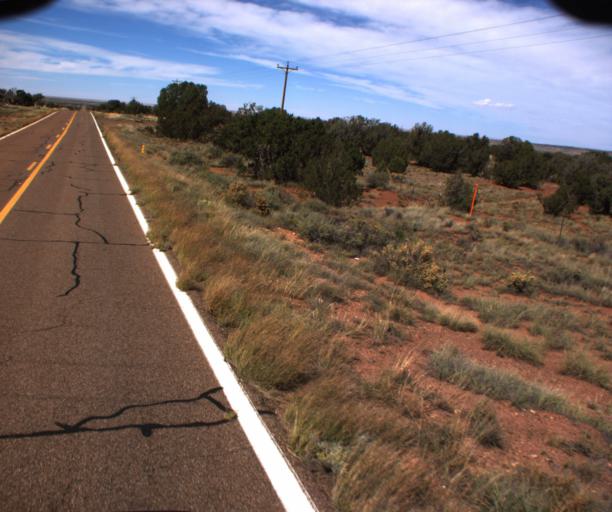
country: US
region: Arizona
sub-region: Apache County
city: Saint Johns
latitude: 34.5863
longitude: -109.6438
